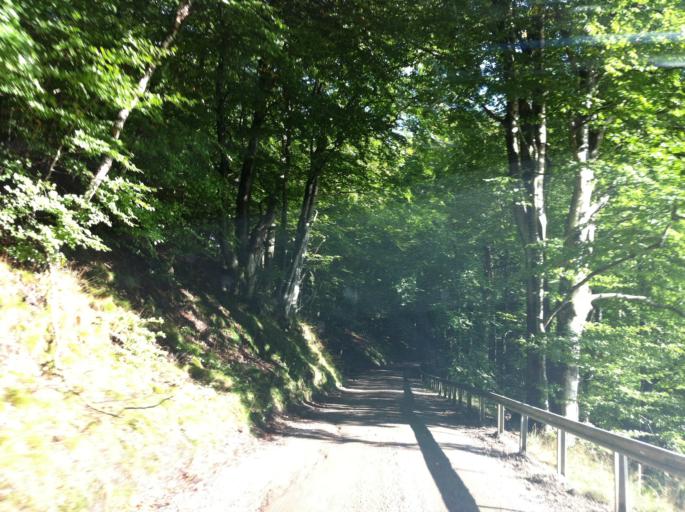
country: SE
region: Skane
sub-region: Perstorps Kommun
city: Perstorp
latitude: 56.1370
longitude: 13.5372
